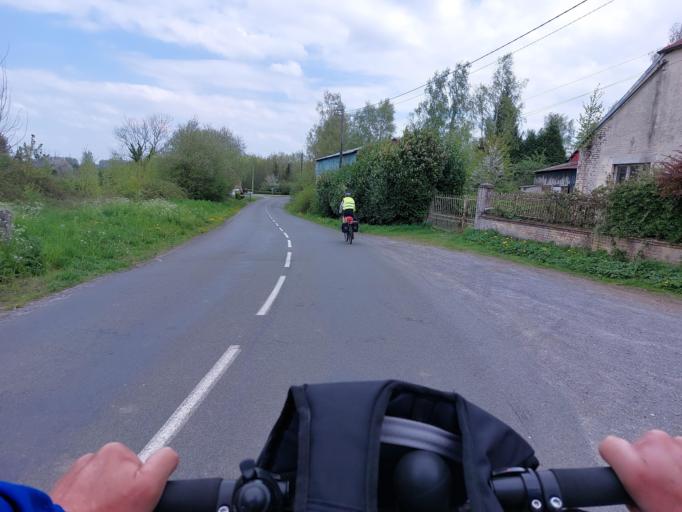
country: FR
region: Nord-Pas-de-Calais
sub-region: Departement du Nord
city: La Longueville
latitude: 50.2770
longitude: 3.8769
